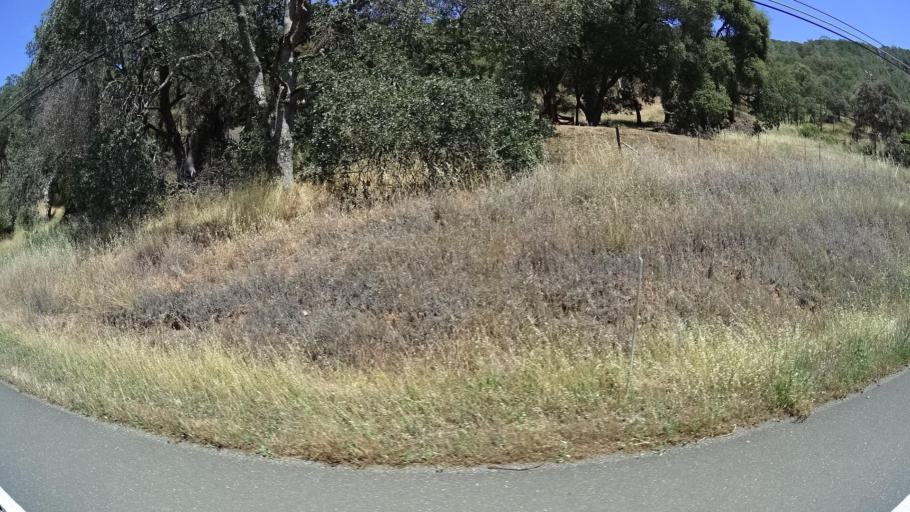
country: US
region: California
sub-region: Lake County
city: Soda Bay
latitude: 39.0389
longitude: -122.7456
